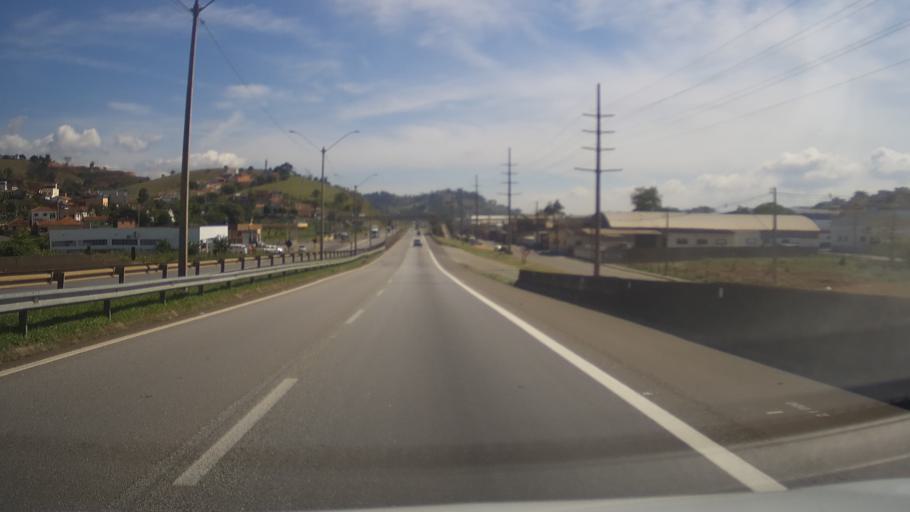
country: BR
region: Minas Gerais
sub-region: Cambui
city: Cambui
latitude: -22.6079
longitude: -46.0605
